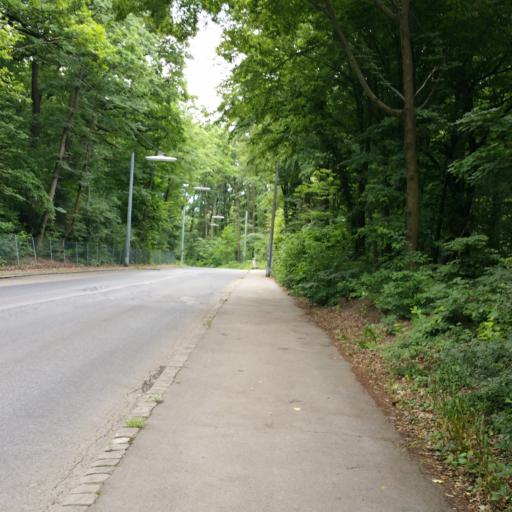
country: AT
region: Vienna
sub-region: Wien Stadt
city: Vienna
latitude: 48.2176
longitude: 16.2784
